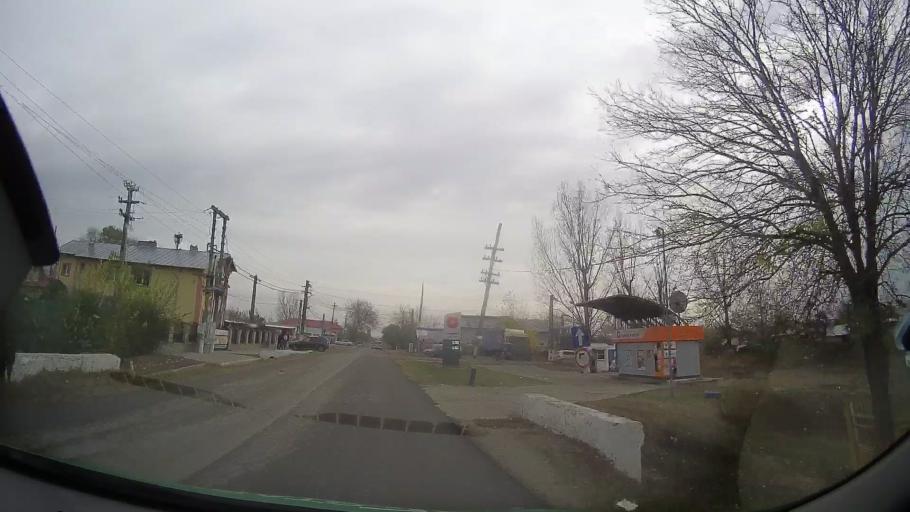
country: RO
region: Prahova
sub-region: Comuna Dumbrava
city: Dumbrava
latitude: 44.8741
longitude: 26.1881
